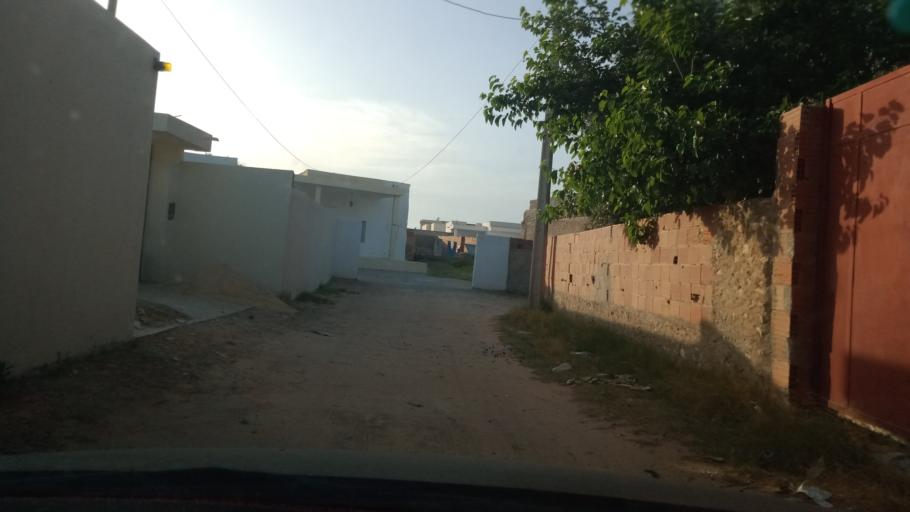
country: TN
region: Safaqis
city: Al Qarmadah
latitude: 34.8185
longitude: 10.7477
